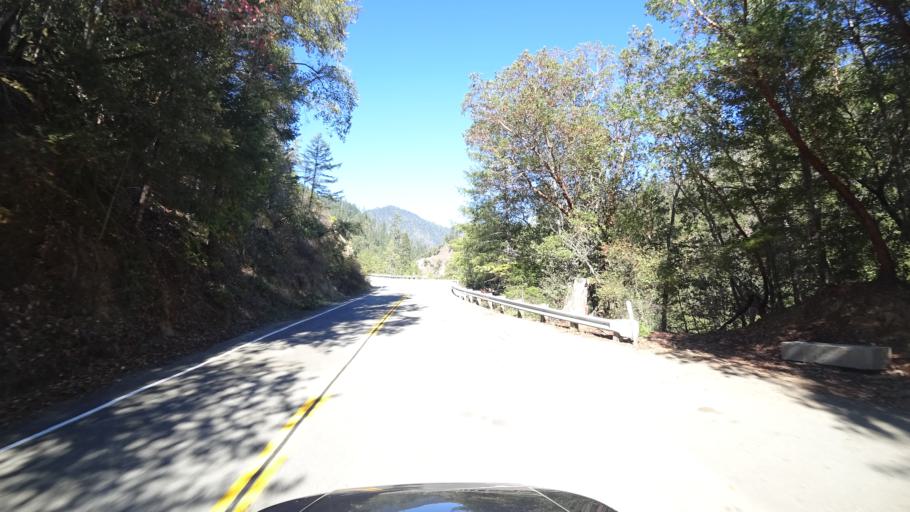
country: US
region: California
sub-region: Siskiyou County
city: Happy Camp
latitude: 41.3581
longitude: -123.4107
